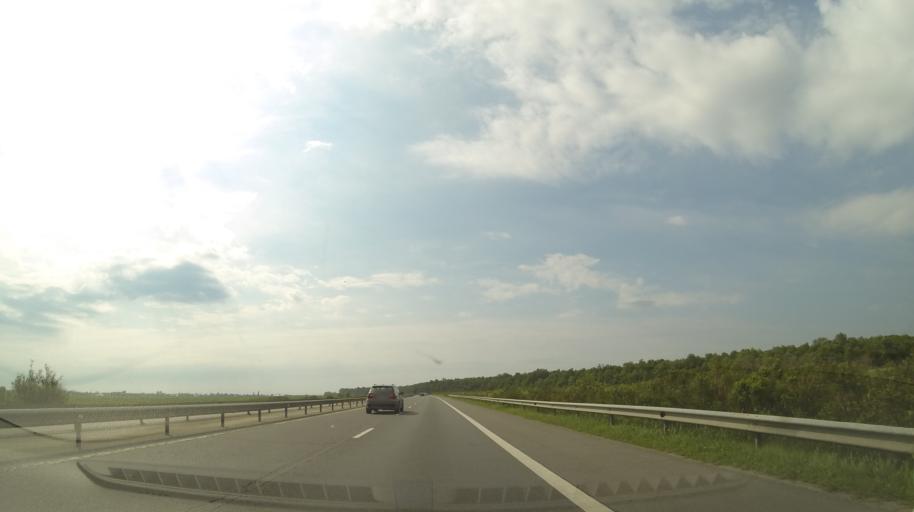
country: RO
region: Dambovita
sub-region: Comuna Corbii Mari
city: Grozavesti
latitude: 44.5899
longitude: 25.4628
